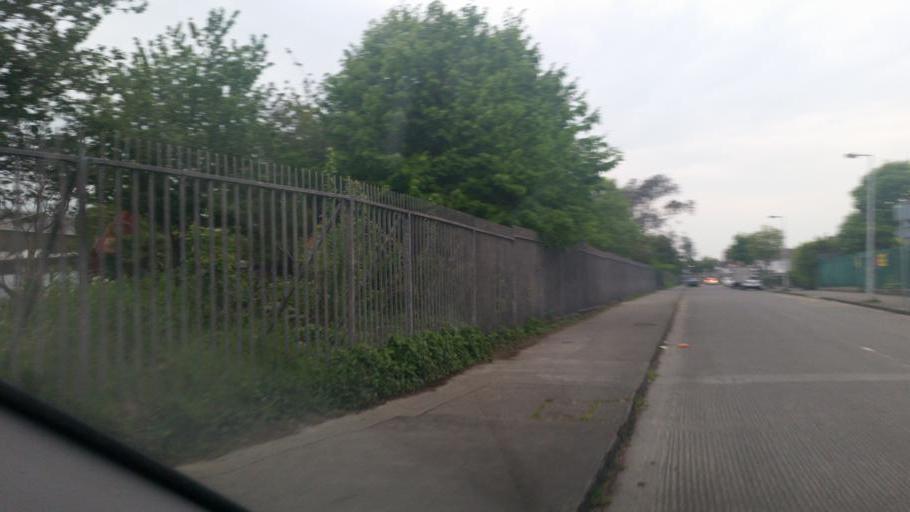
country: IE
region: Leinster
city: Donaghmede
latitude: 53.3864
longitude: -6.1574
